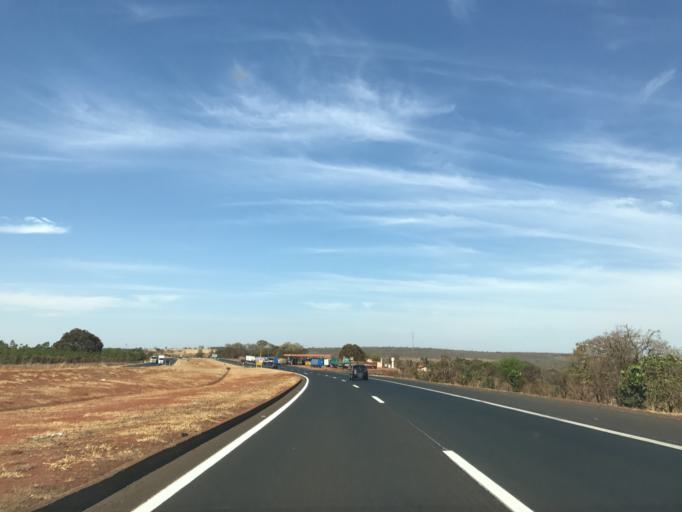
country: BR
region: Minas Gerais
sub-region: Monte Alegre De Minas
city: Monte Alegre de Minas
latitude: -18.8134
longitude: -49.0867
